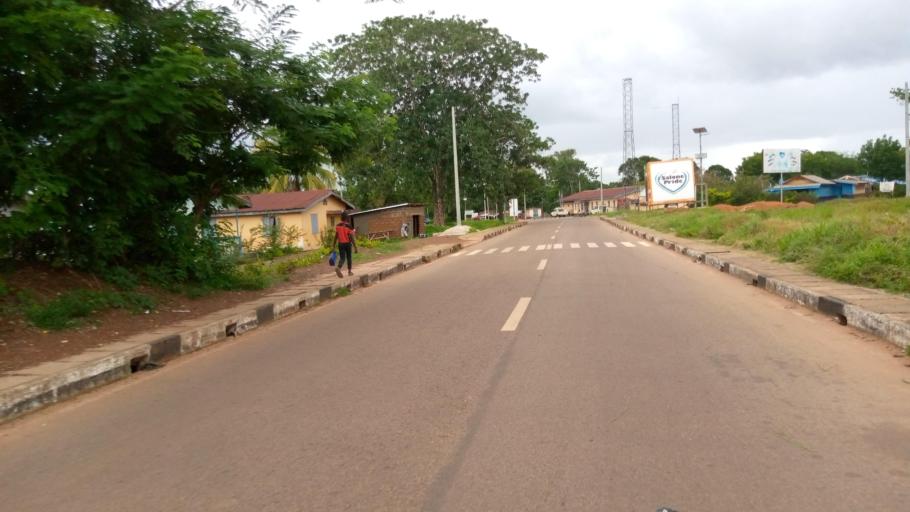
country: SL
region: Southern Province
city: Moyamba
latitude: 8.1619
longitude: -12.4381
